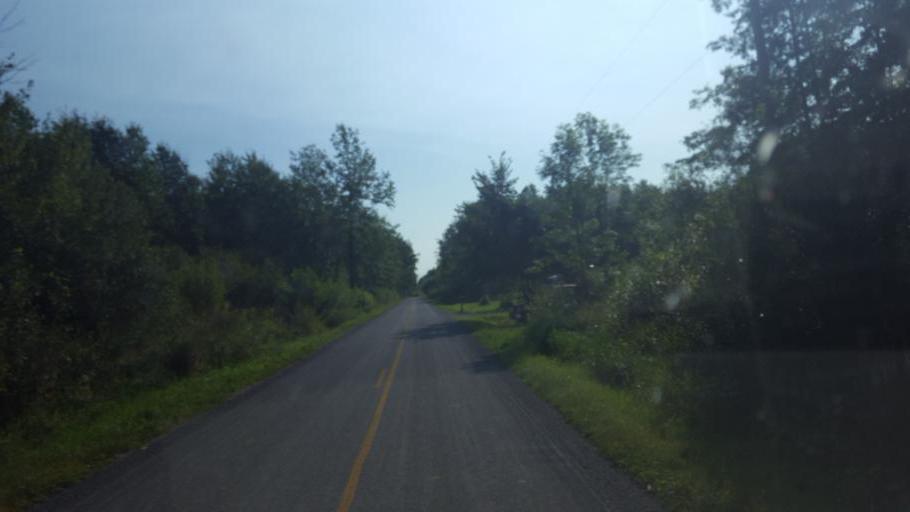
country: US
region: Ohio
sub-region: Ashtabula County
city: Orwell
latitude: 41.4755
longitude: -80.9086
